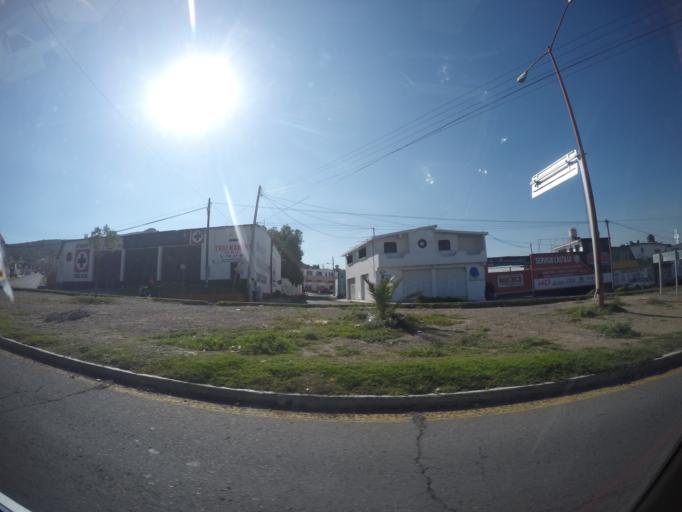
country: MX
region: Hidalgo
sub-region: Mineral de la Reforma
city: Rio de la Soledad
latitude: 20.1141
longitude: -98.7147
